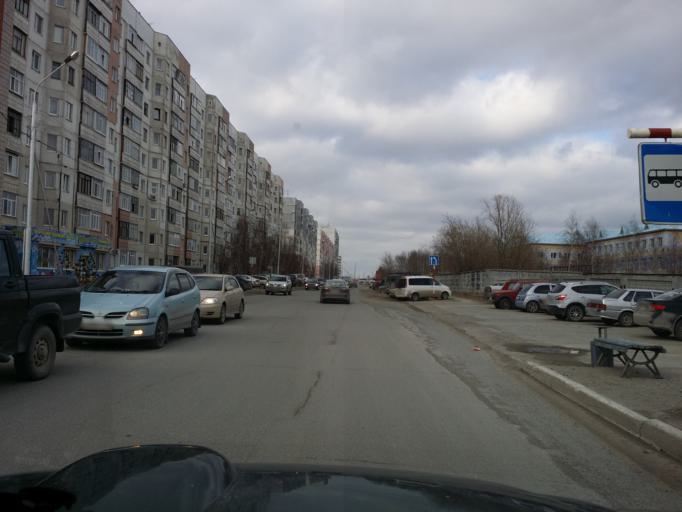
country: RU
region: Khanty-Mansiyskiy Avtonomnyy Okrug
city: Nizhnevartovsk
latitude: 60.9431
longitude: 76.6102
